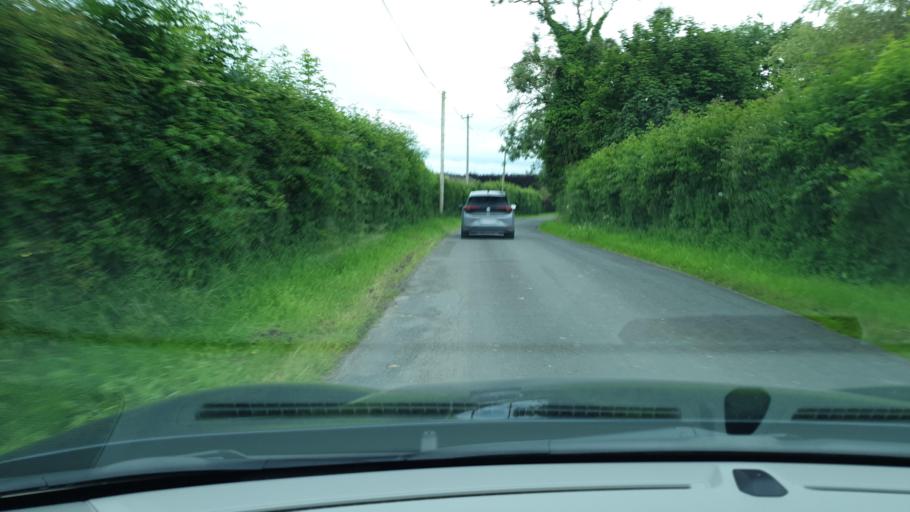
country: IE
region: Leinster
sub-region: An Mhi
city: Dunshaughlin
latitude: 53.5244
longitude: -6.5249
